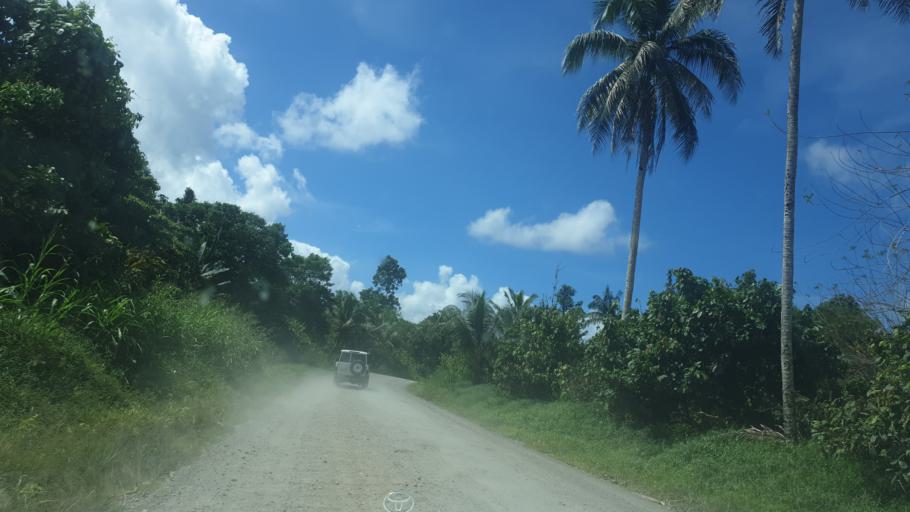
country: PG
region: Bougainville
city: Panguna
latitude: -6.7380
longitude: 155.6670
